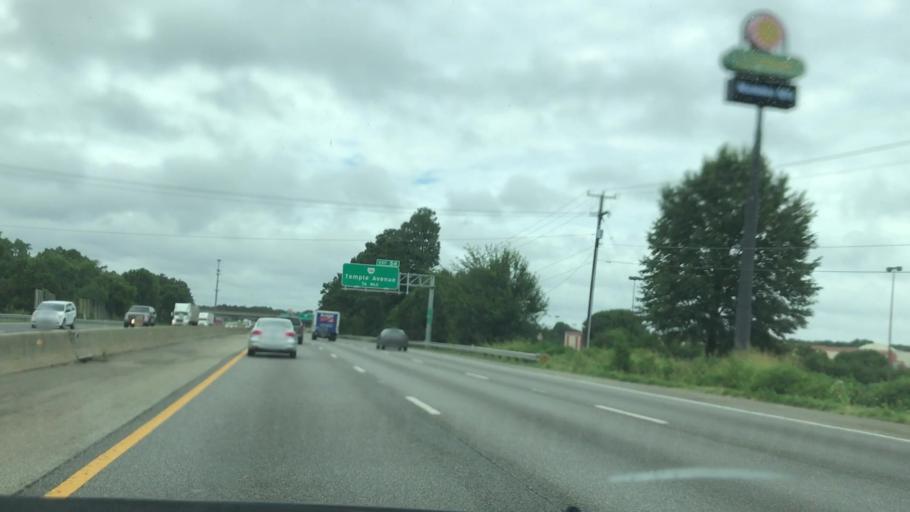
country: US
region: Virginia
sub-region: City of Colonial Heights
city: Colonial Heights
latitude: 37.2509
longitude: -77.3944
